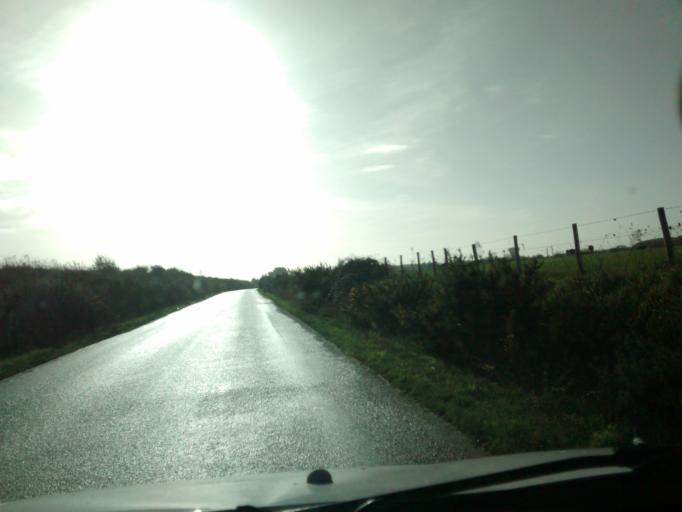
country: FR
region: Brittany
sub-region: Departement d'Ille-et-Vilaine
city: Betton
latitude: 48.1521
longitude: -1.6248
